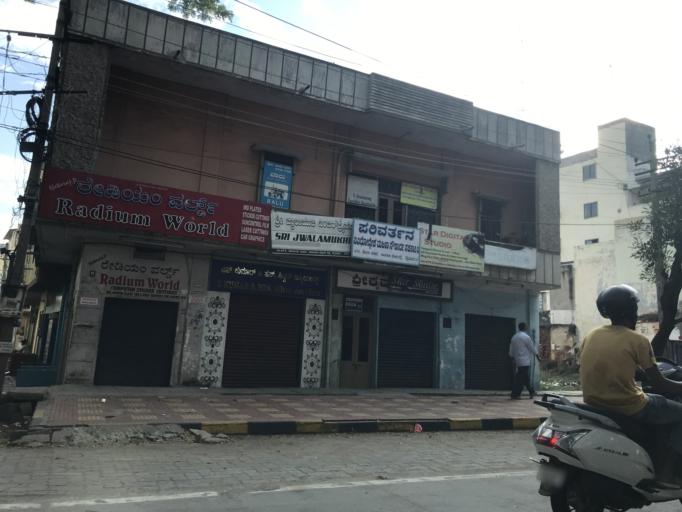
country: IN
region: Karnataka
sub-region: Mysore
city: Mysore
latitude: 12.3017
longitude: 76.6503
